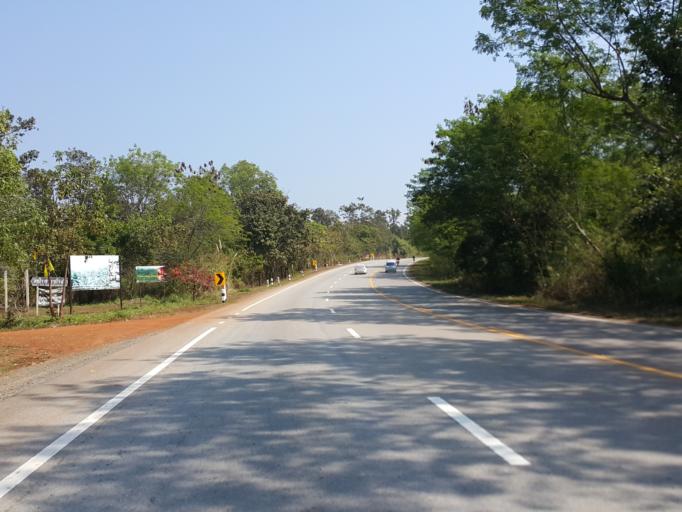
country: TH
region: Chiang Mai
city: Mae On
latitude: 18.9054
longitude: 99.2045
